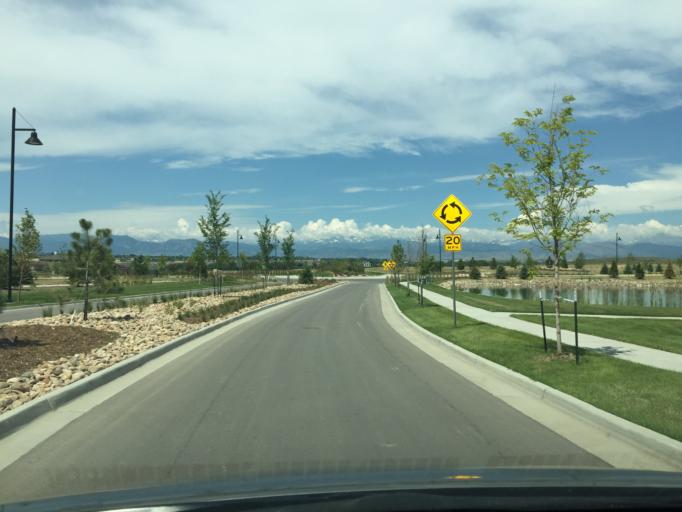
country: US
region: Colorado
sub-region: Boulder County
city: Erie
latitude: 40.0472
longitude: -105.0338
